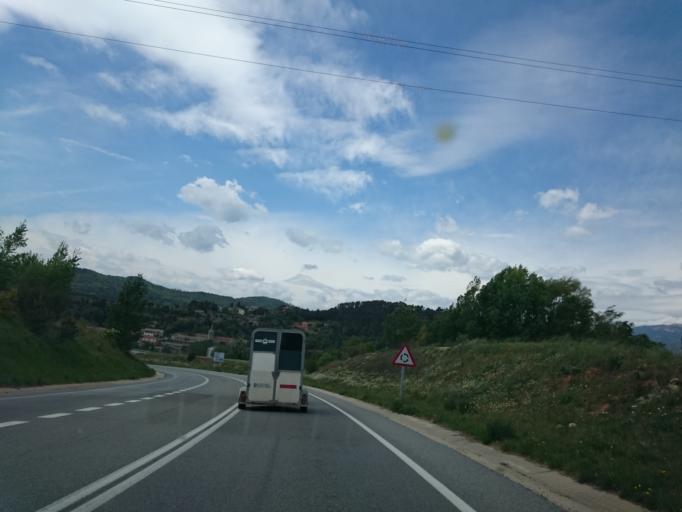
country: ES
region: Catalonia
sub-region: Provincia de Barcelona
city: Gironella
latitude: 42.0484
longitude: 1.8798
